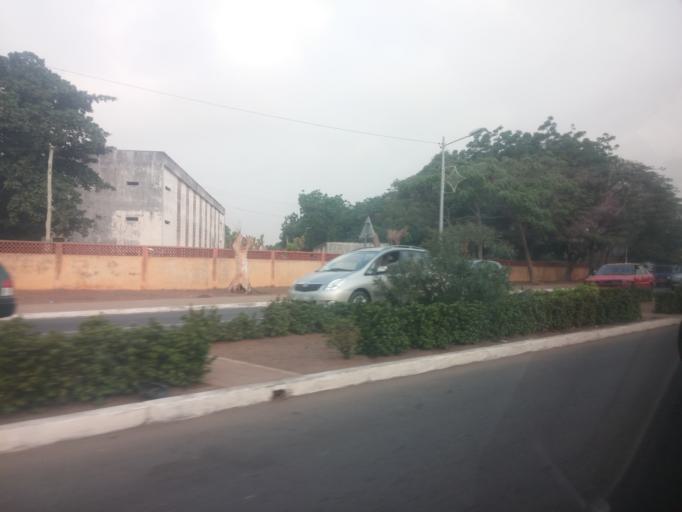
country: TG
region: Maritime
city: Lome
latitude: 6.1501
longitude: 1.2301
